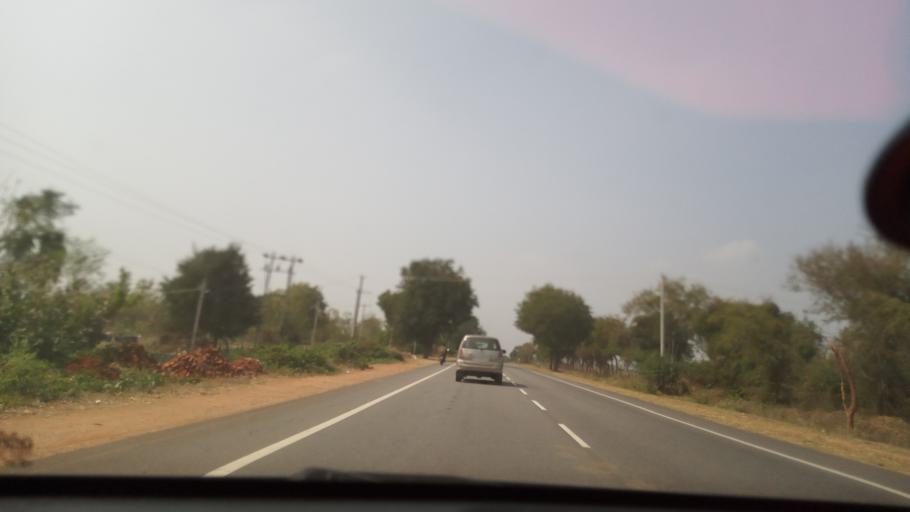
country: IN
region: Karnataka
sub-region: Mysore
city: Nanjangud
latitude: 12.0714
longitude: 76.7446
